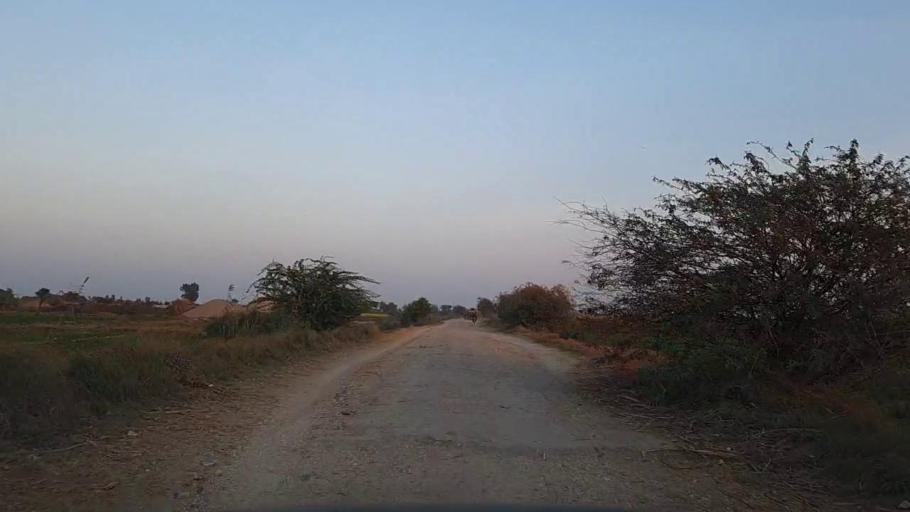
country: PK
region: Sindh
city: Tando Mittha Khan
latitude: 25.9585
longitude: 69.1114
